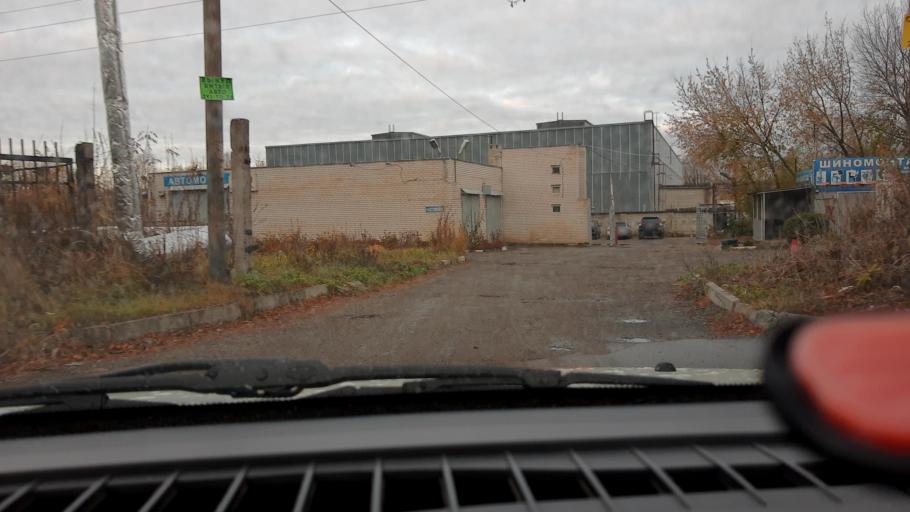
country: RU
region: Nizjnij Novgorod
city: Gorbatovka
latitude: 56.3229
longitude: 43.8642
